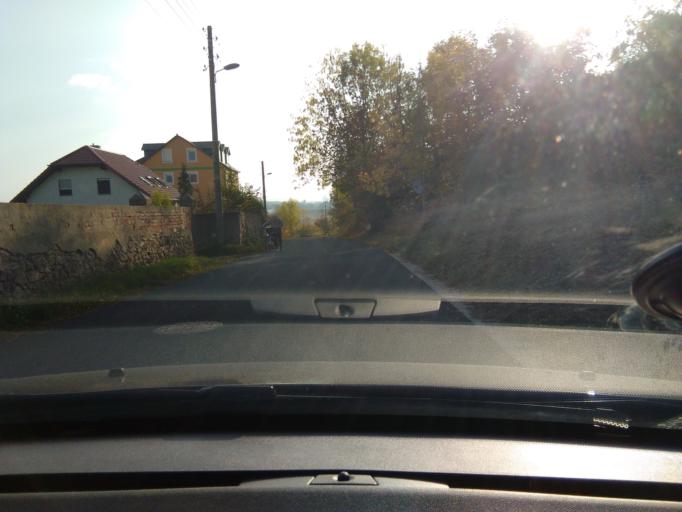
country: DE
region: Saxony
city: Niederau
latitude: 51.1508
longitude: 13.5160
